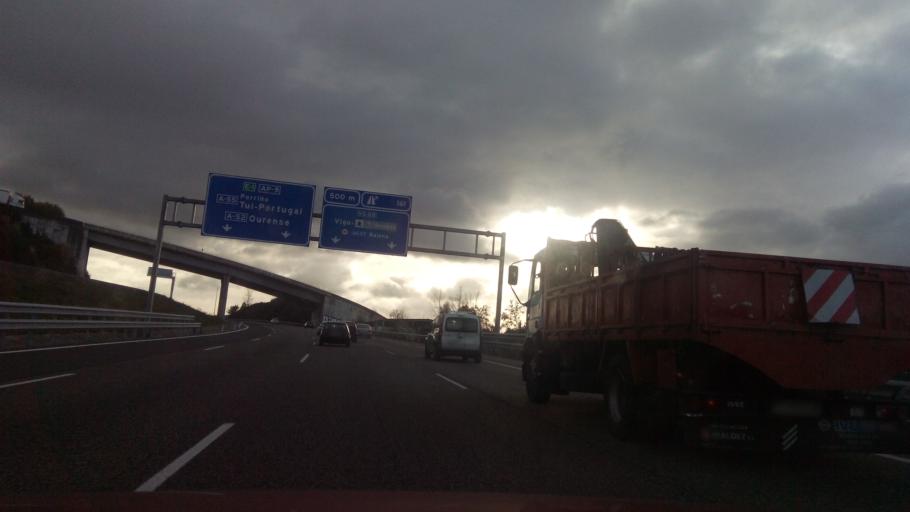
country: ES
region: Galicia
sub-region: Provincia de Pontevedra
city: Vigo
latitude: 42.2074
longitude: -8.6673
